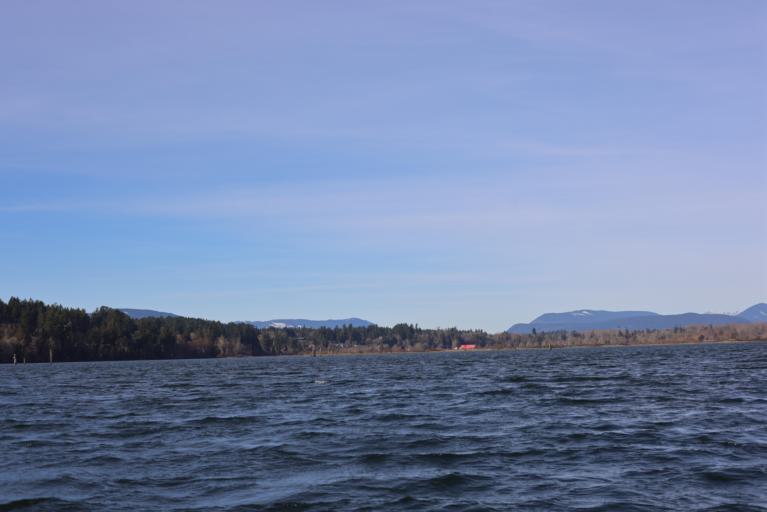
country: CA
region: British Columbia
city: Duncan
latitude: 48.7454
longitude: -123.6228
